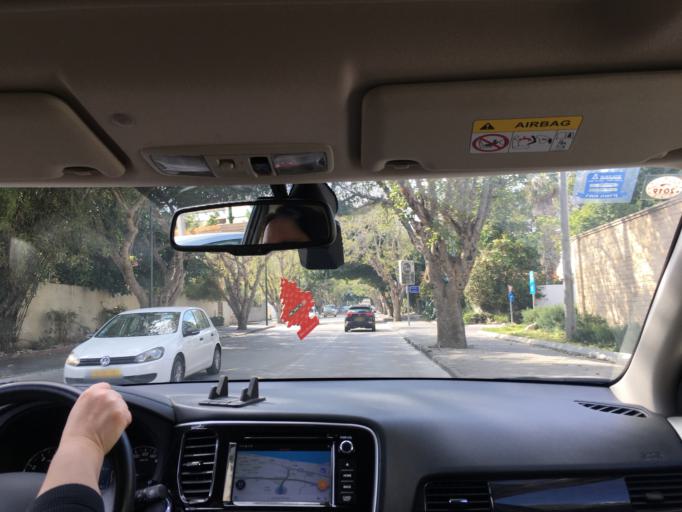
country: IL
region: Tel Aviv
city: Kefar Shemaryahu
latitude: 32.1805
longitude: 34.8138
